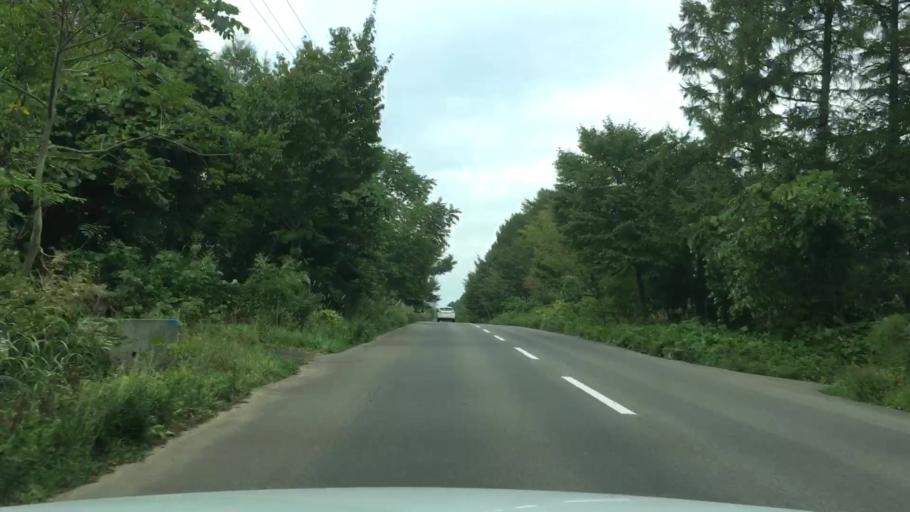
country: JP
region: Aomori
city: Shimokizukuri
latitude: 40.7120
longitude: 140.3280
